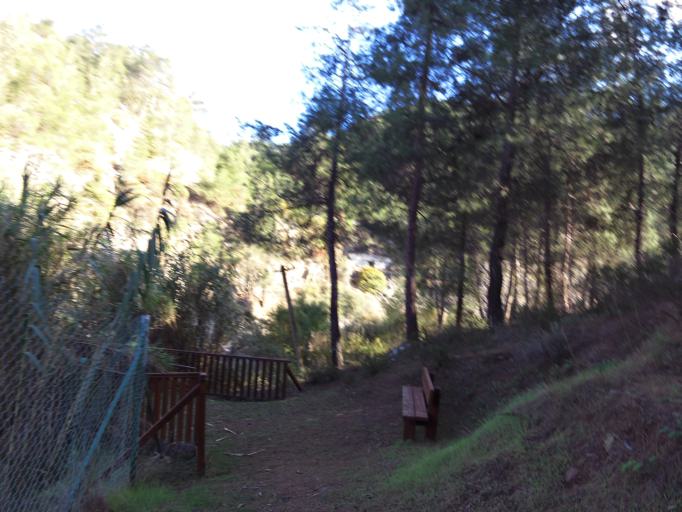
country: CY
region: Limassol
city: Kyperounta
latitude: 35.0024
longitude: 33.0387
